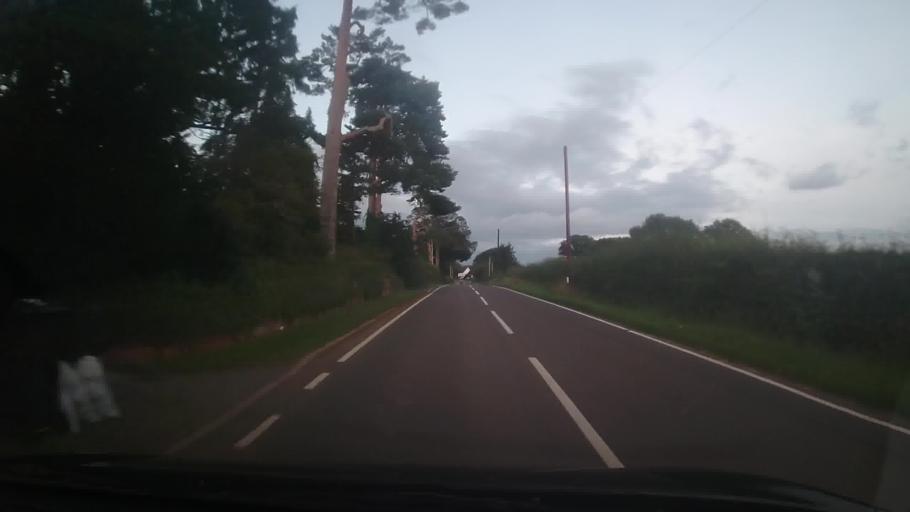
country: GB
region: England
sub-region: Shropshire
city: Petton
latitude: 52.8074
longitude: -2.7999
